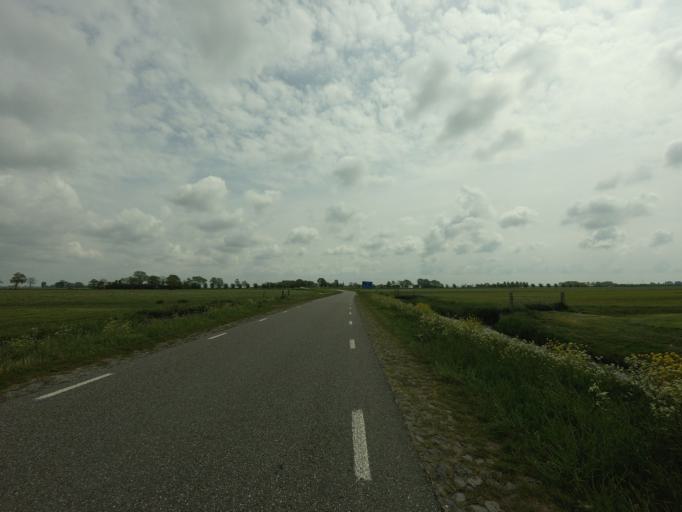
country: NL
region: Friesland
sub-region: Sudwest Fryslan
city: Bolsward
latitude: 53.0952
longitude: 5.5299
